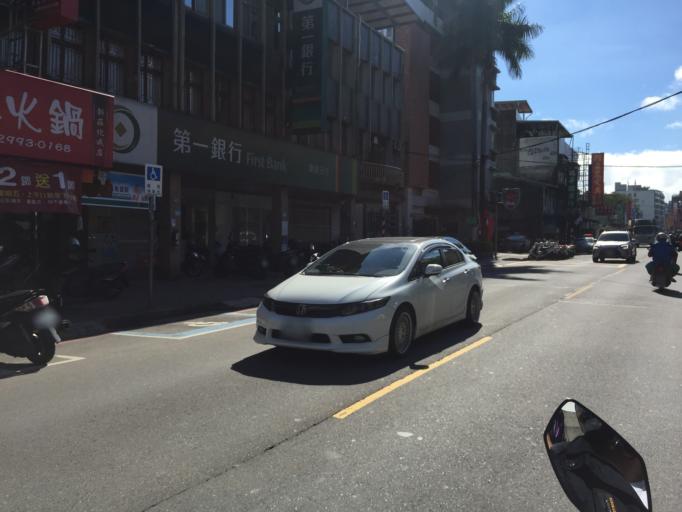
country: TW
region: Taipei
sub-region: Taipei
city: Banqiao
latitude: 25.0488
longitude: 121.4658
